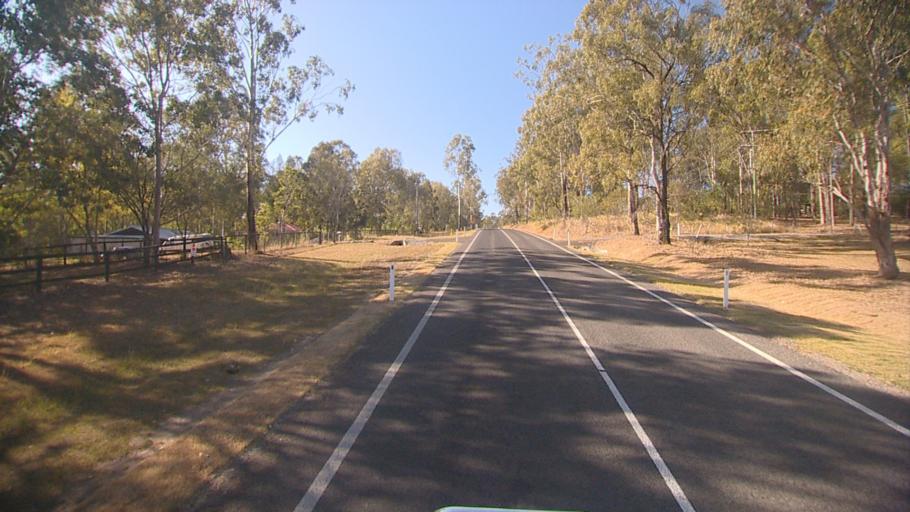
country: AU
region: Queensland
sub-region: Logan
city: Cedar Vale
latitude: -27.8613
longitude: 152.9809
